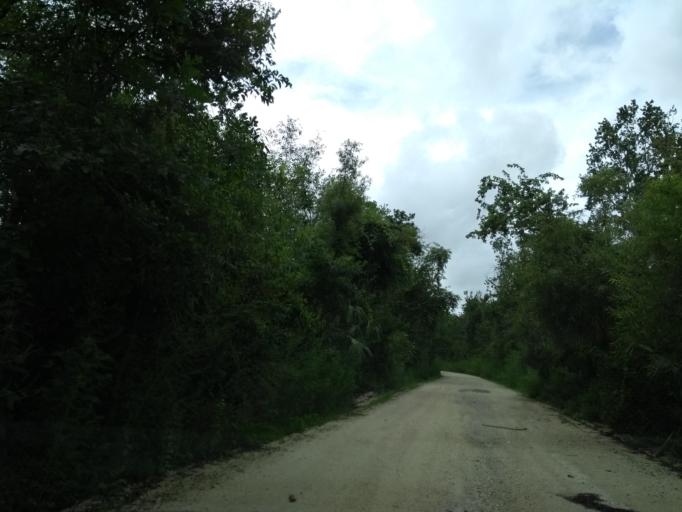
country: US
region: Florida
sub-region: Collier County
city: Lely Resort
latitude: 25.9821
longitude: -81.4110
